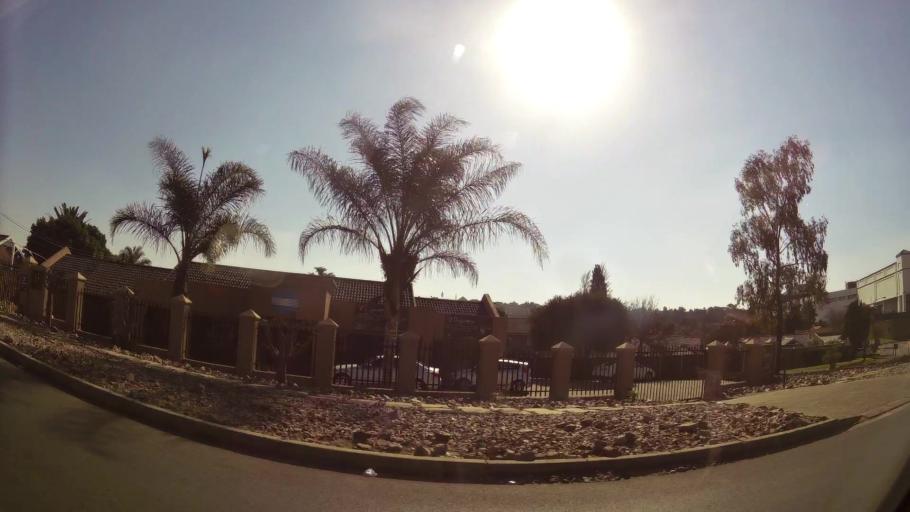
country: ZA
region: Gauteng
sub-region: City of Johannesburg Metropolitan Municipality
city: Johannesburg
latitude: -26.2678
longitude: 28.0584
